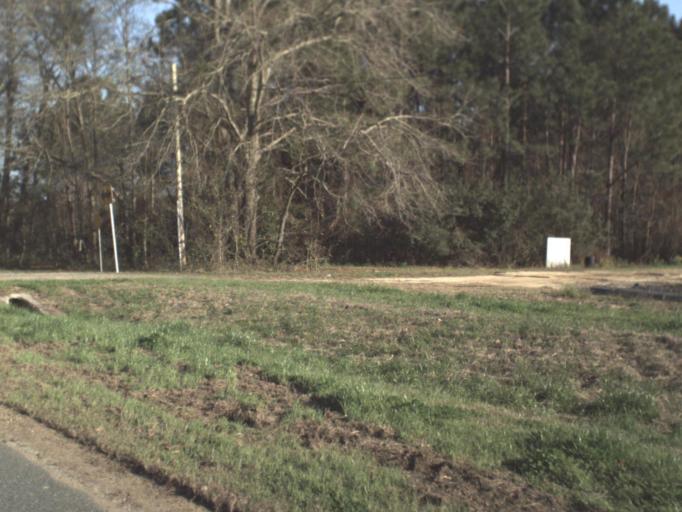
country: US
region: Florida
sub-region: Jackson County
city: Sneads
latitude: 30.7196
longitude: -85.0539
